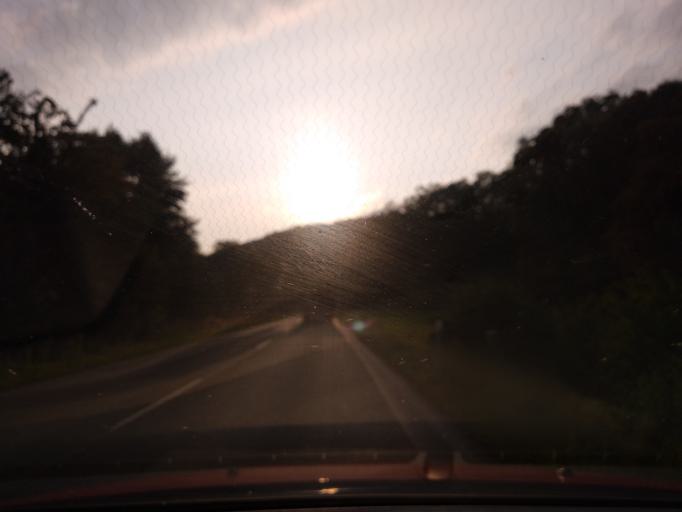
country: DE
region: North Rhine-Westphalia
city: Beverungen
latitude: 51.6512
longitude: 9.3331
